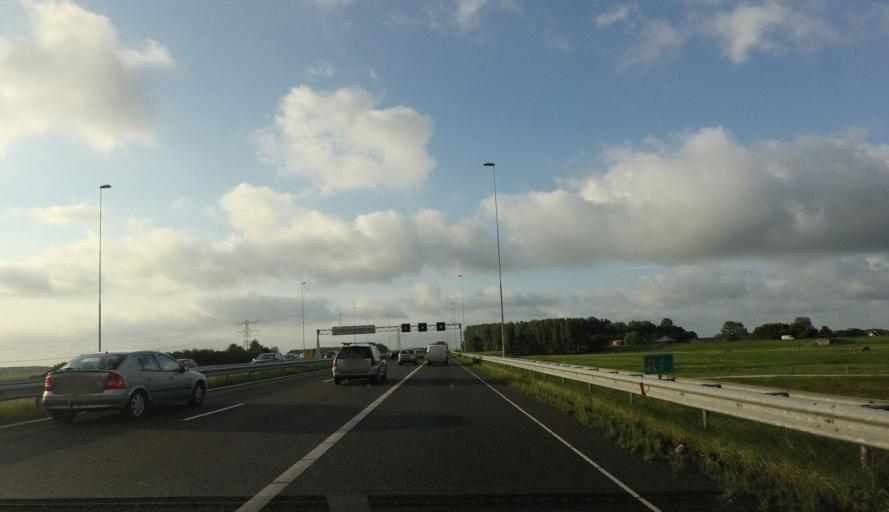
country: NL
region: North Holland
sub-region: Gemeente Haarlem
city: Haarlem
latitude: 52.4094
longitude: 4.7012
